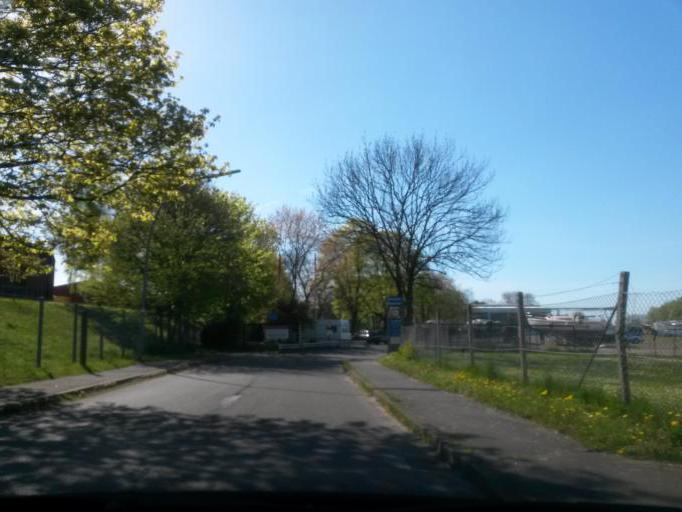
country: DE
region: Schleswig-Holstein
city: Wedel
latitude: 53.5730
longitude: 9.6878
